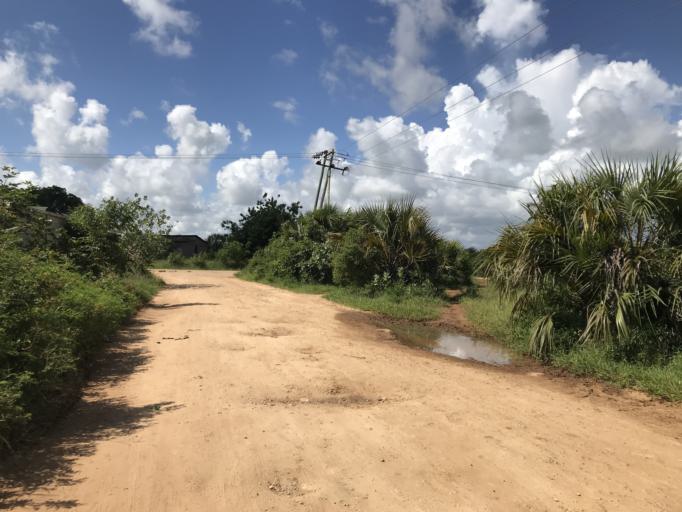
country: TZ
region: Dar es Salaam
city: Dar es Salaam
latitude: -6.8810
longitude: 39.4398
